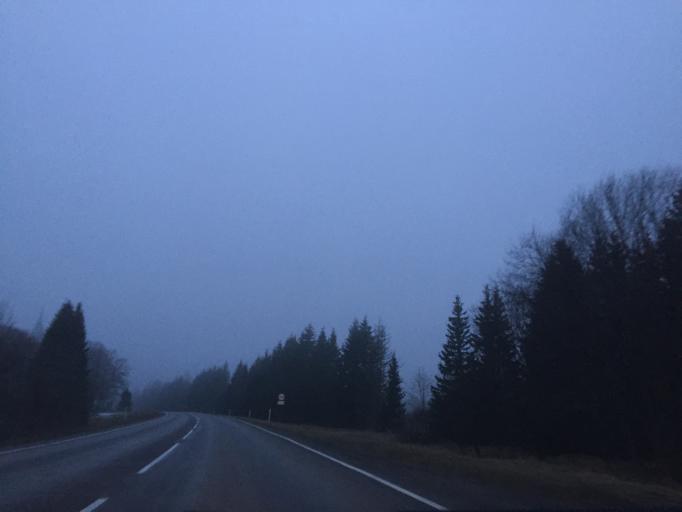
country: EE
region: Laeaene
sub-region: Lihula vald
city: Lihula
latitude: 58.6388
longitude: 23.6913
